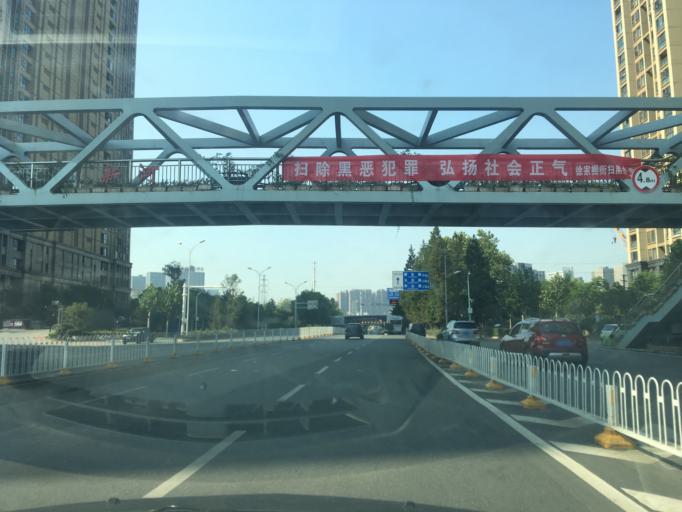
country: CN
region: Hubei
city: Jiang'an
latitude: 30.5709
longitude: 114.3147
